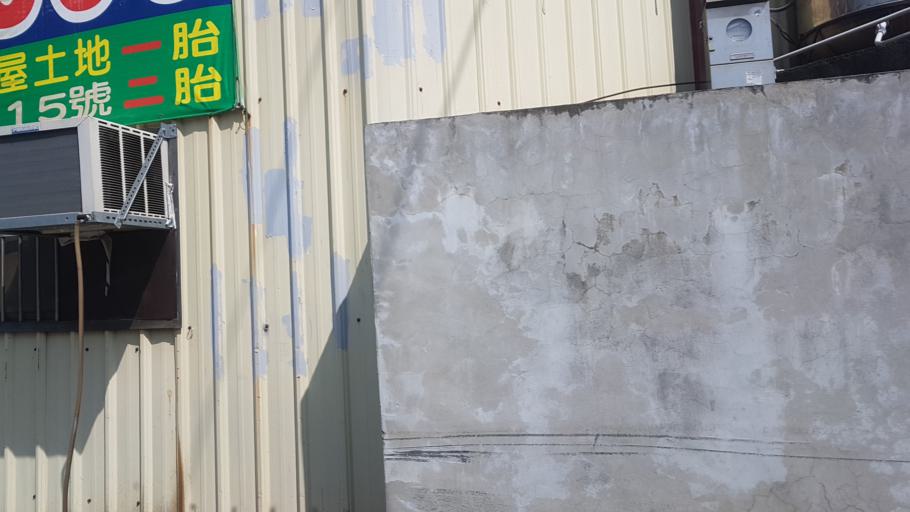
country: TW
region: Taiwan
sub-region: Tainan
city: Tainan
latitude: 22.9374
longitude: 120.2479
